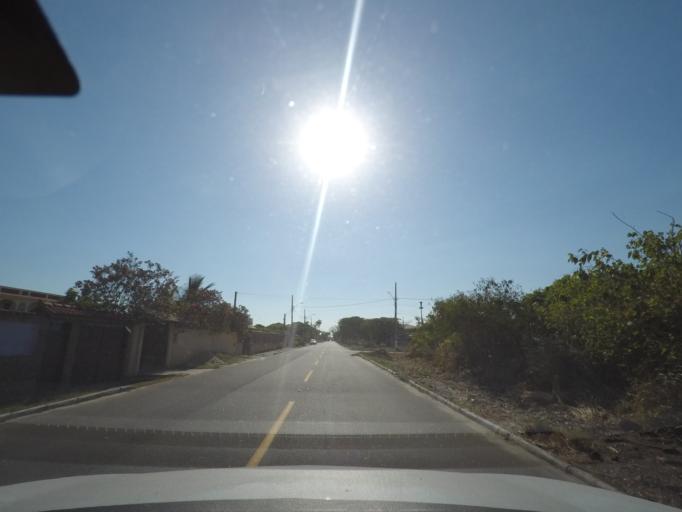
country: BR
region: Rio de Janeiro
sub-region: Marica
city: Marica
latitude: -22.9702
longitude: -42.9132
